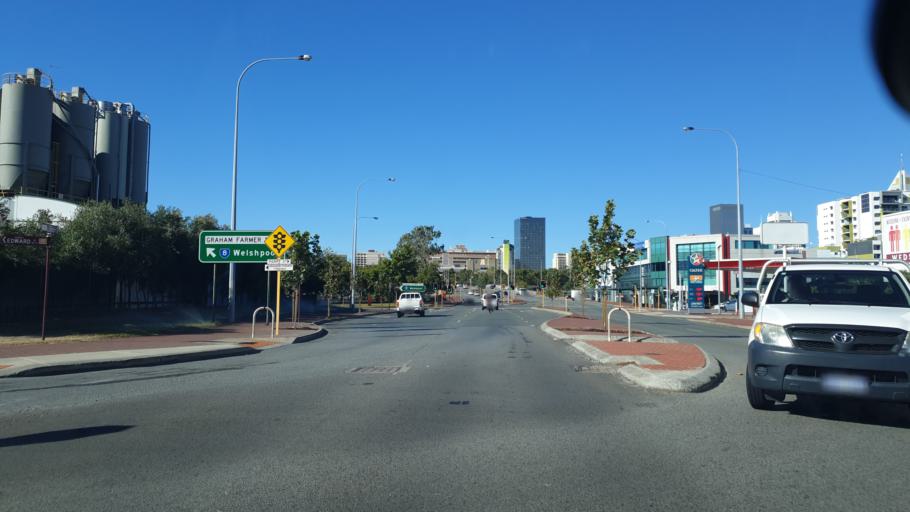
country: AU
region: Western Australia
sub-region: Cambridge
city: Perth
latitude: -31.9480
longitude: 115.8703
